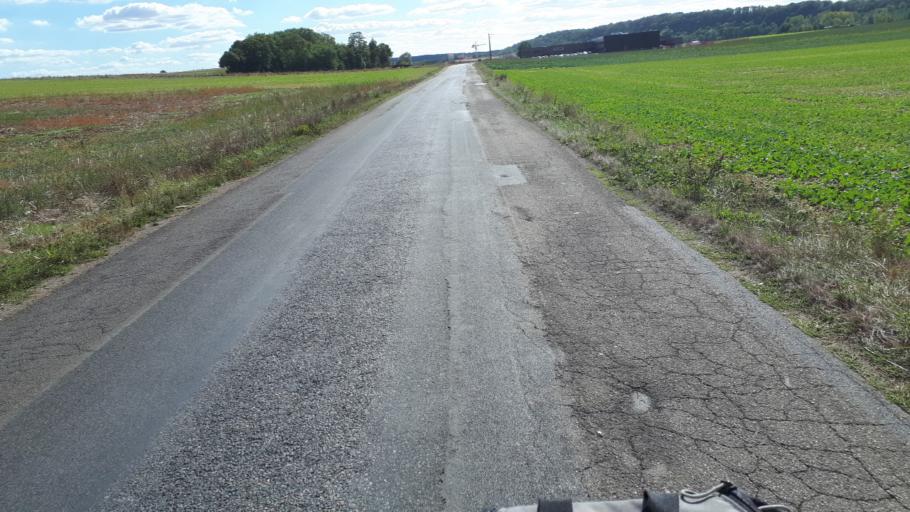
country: FR
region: Centre
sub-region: Departement du Loir-et-Cher
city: Villiers-sur-Loir
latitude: 47.8032
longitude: 0.9686
